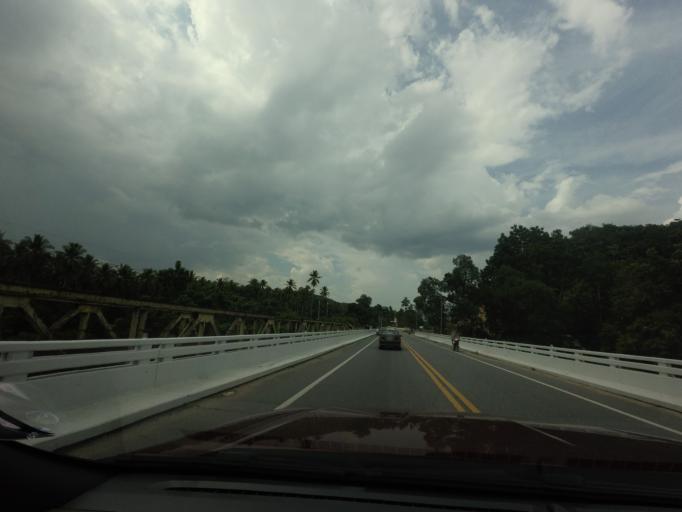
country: TH
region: Yala
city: Ban Nang Sata
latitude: 6.2784
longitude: 101.2898
